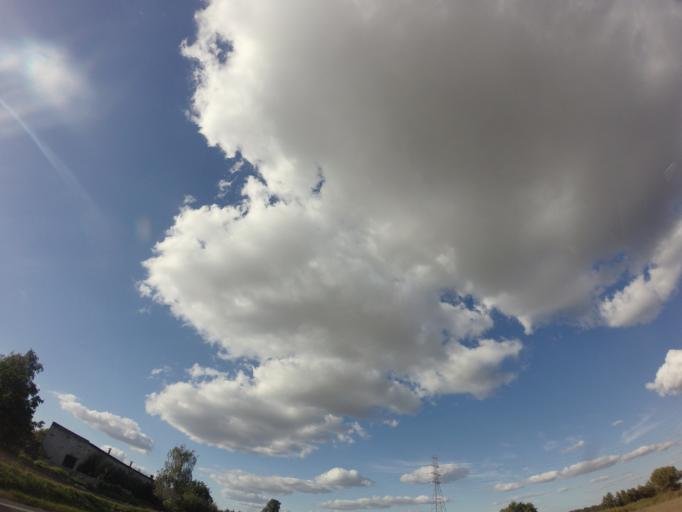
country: PL
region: Greater Poland Voivodeship
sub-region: Powiat koscianski
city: Smigiel
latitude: 52.0223
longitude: 16.5375
